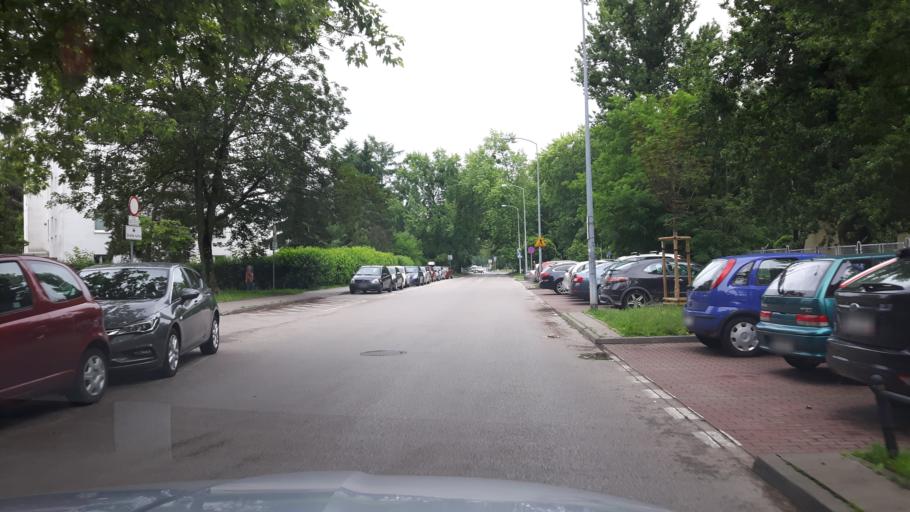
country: PL
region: Masovian Voivodeship
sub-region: Warszawa
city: Zoliborz
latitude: 52.2628
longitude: 20.9662
